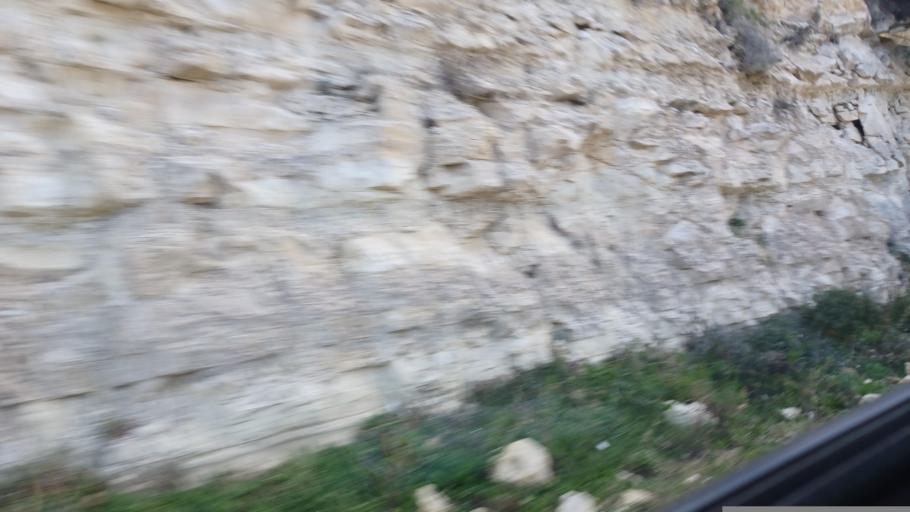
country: CY
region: Limassol
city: Pachna
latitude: 34.8209
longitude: 32.7797
